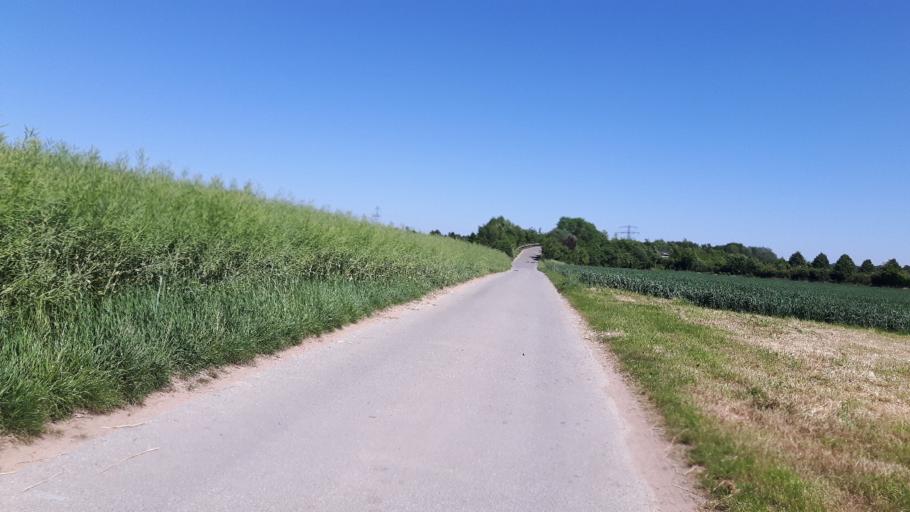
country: DE
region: North Rhine-Westphalia
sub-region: Regierungsbezirk Dusseldorf
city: Ratingen
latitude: 51.3105
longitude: 6.7704
